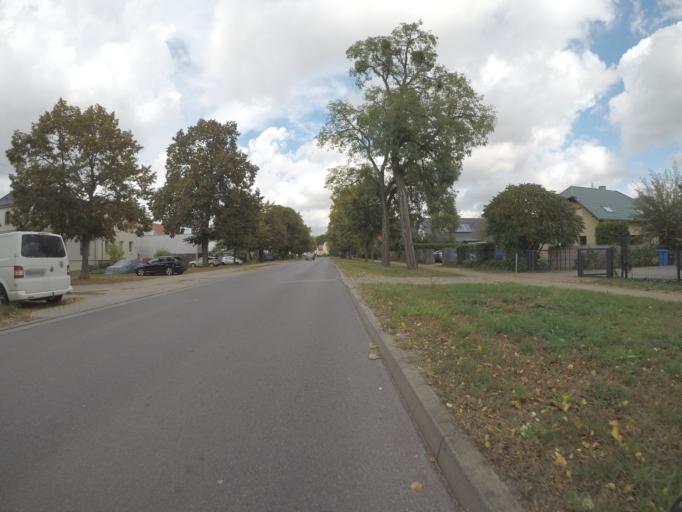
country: DE
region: Brandenburg
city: Altlandsberg
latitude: 52.5695
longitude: 13.7287
